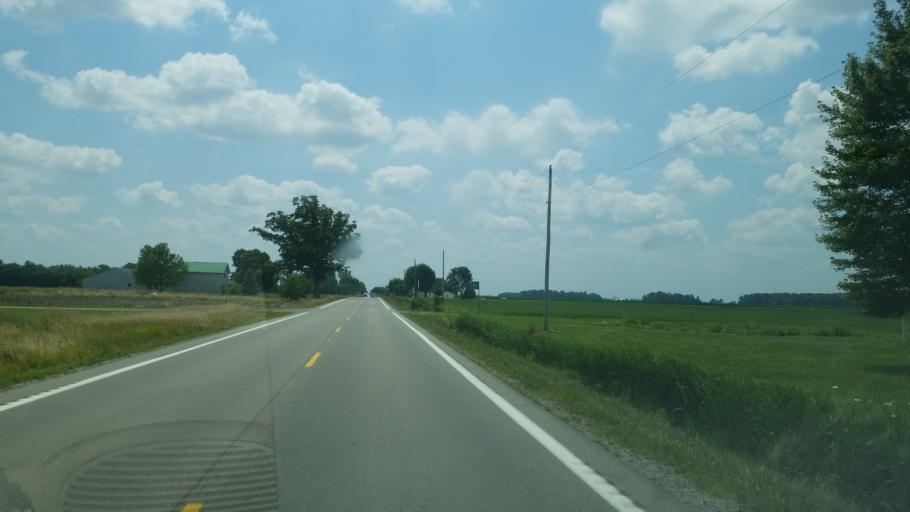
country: US
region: Ohio
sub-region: Henry County
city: Deshler
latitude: 41.2769
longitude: -83.9406
